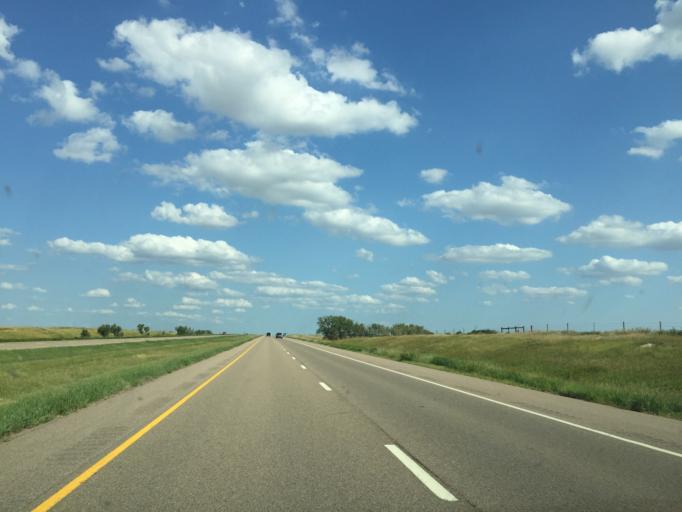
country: US
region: Kansas
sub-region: Gove County
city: Gove
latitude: 39.0932
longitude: -100.3170
